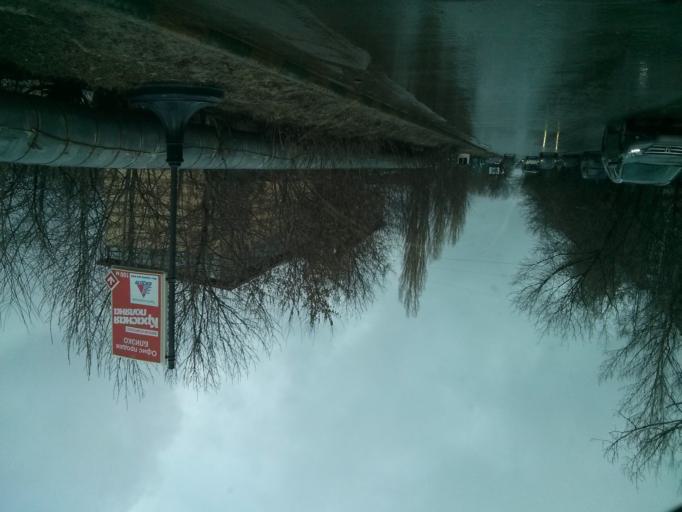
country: RU
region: Nizjnij Novgorod
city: Bor
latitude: 56.3156
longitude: 44.0550
